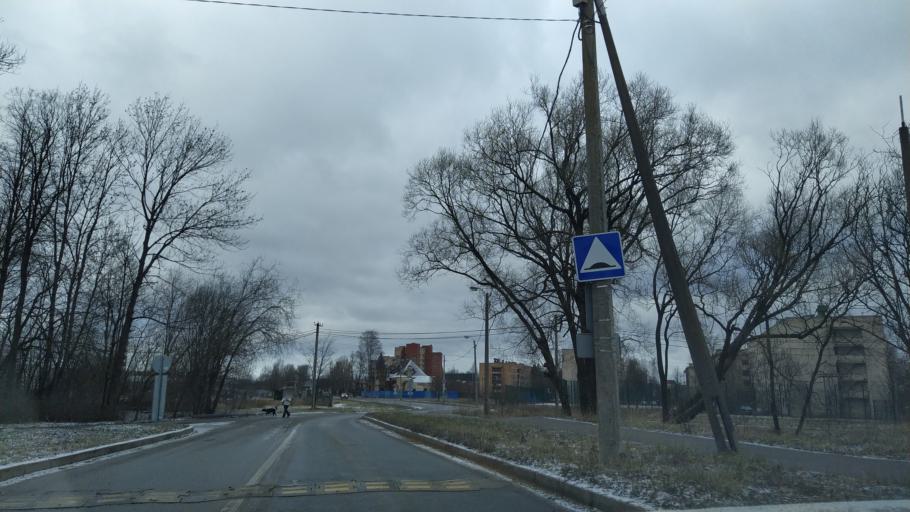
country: RU
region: St.-Petersburg
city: Pushkin
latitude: 59.7294
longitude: 30.3859
